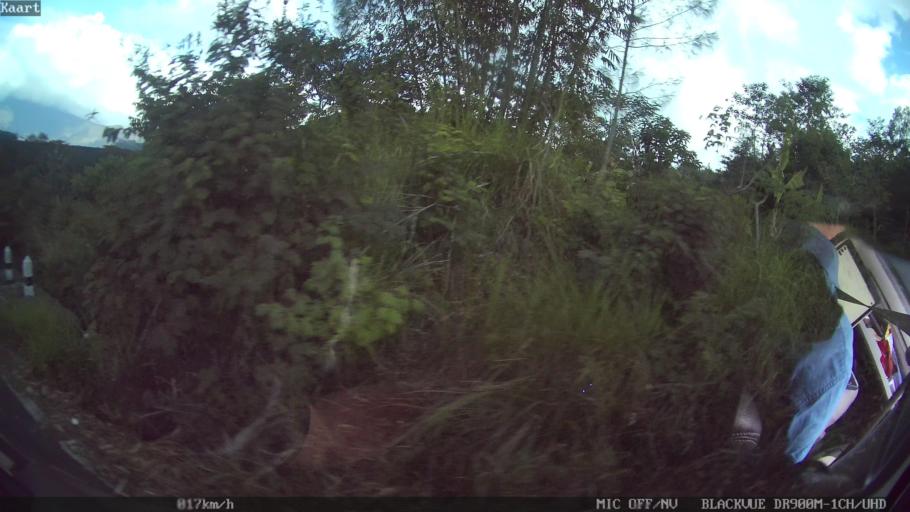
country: ID
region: Bali
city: Banjar Kedisan
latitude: -8.2584
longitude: 115.3491
